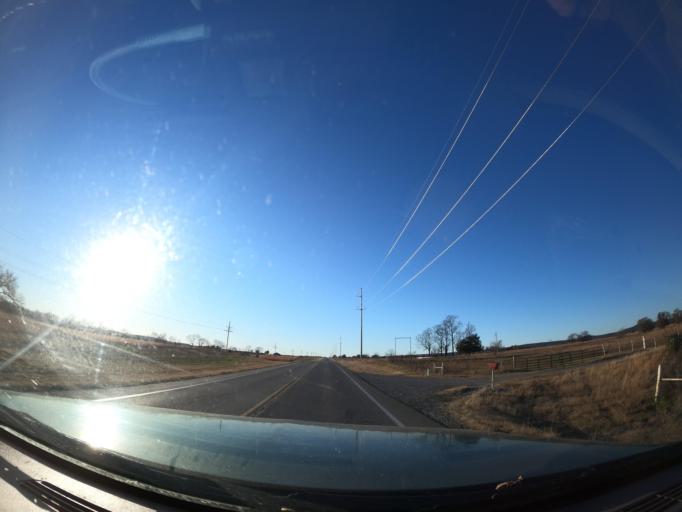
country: US
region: Oklahoma
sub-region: Latimer County
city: Wilburton
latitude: 34.9130
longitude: -95.4059
